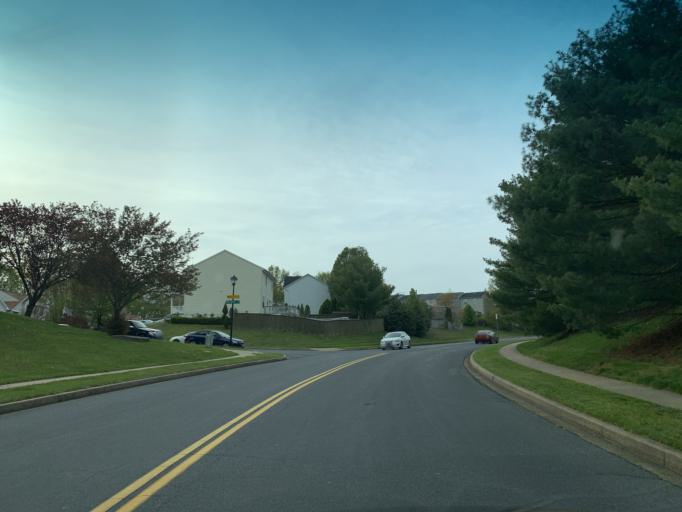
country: US
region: Maryland
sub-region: Harford County
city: Riverside
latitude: 39.4765
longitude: -76.2534
